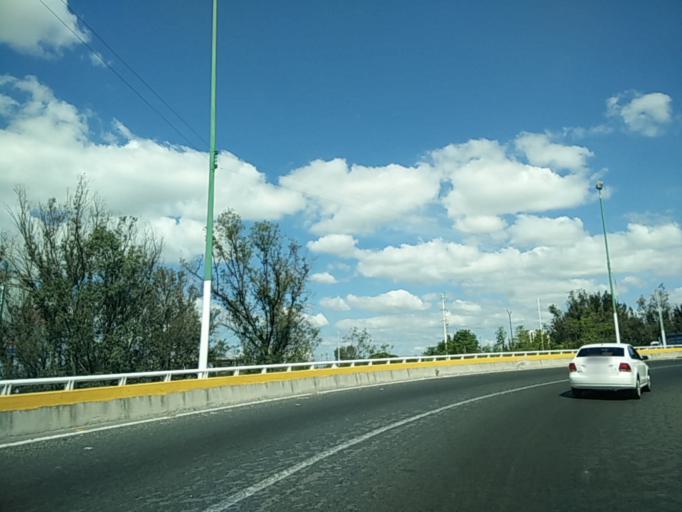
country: MX
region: Jalisco
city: Zapopan2
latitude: 20.6960
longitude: -103.4562
